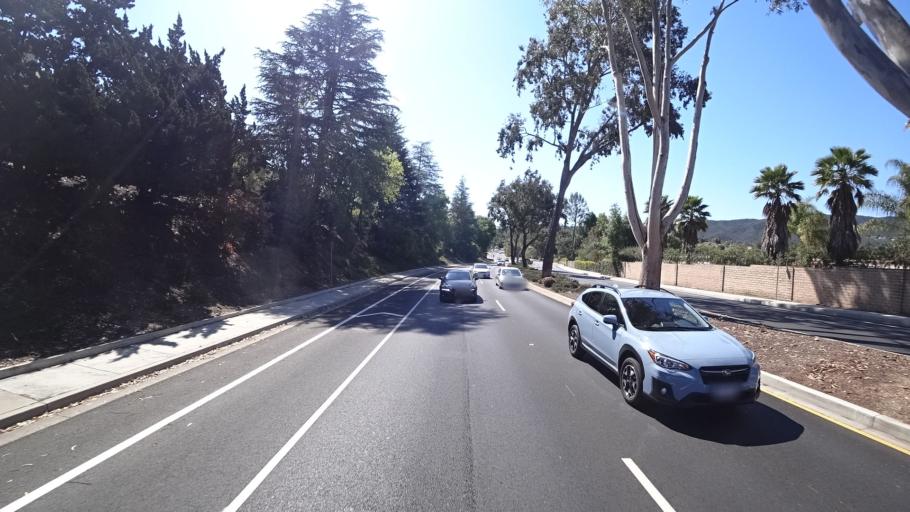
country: US
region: California
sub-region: Ventura County
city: Casa Conejo
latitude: 34.1879
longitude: -118.8934
